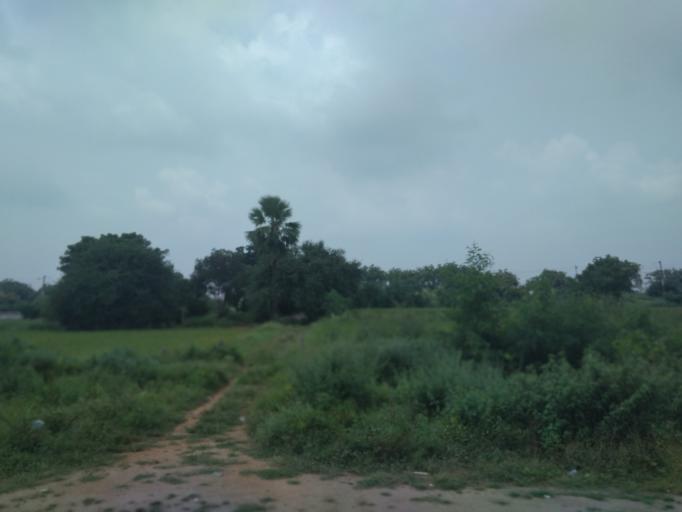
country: IN
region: Telangana
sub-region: Warangal
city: Jangaon
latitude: 17.6784
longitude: 79.1015
